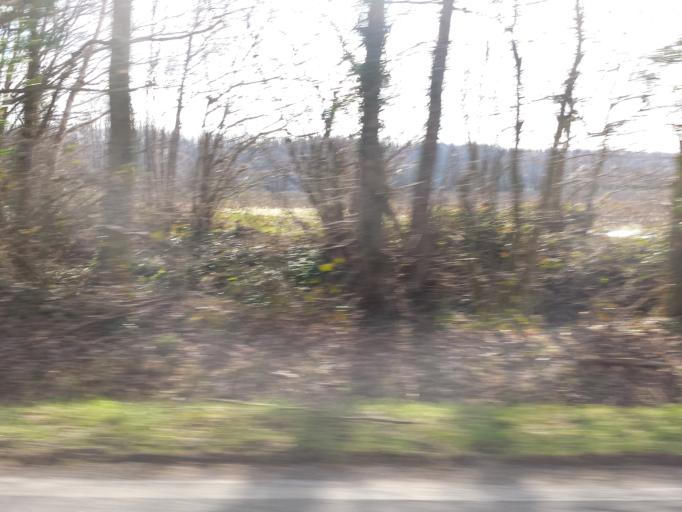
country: DE
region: North Rhine-Westphalia
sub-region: Regierungsbezirk Munster
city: Havixbeck
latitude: 51.9454
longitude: 7.4769
